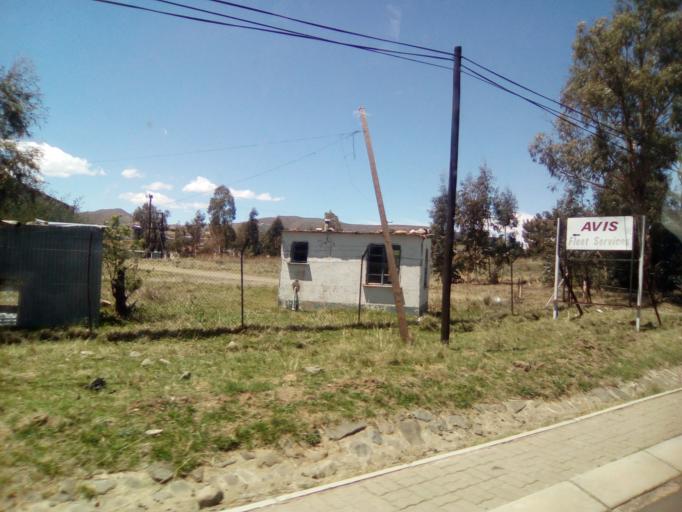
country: LS
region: Qacha's Nek
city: Qacha's Nek
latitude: -30.1041
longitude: 28.6706
